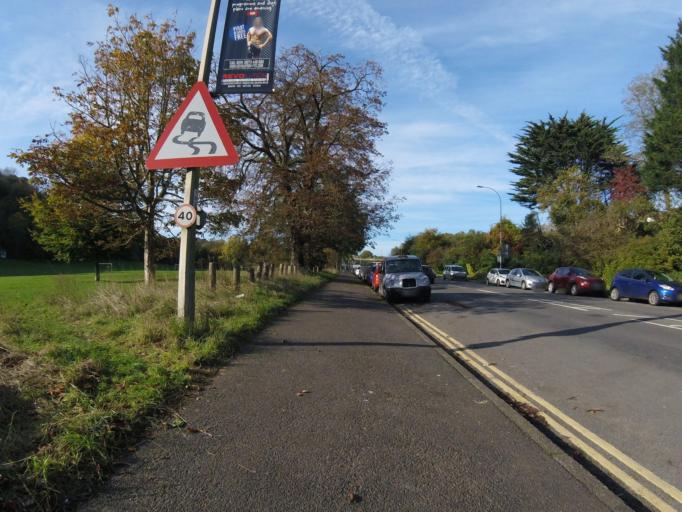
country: GB
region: England
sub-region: Brighton and Hove
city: Hove
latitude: 50.8660
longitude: -0.1536
